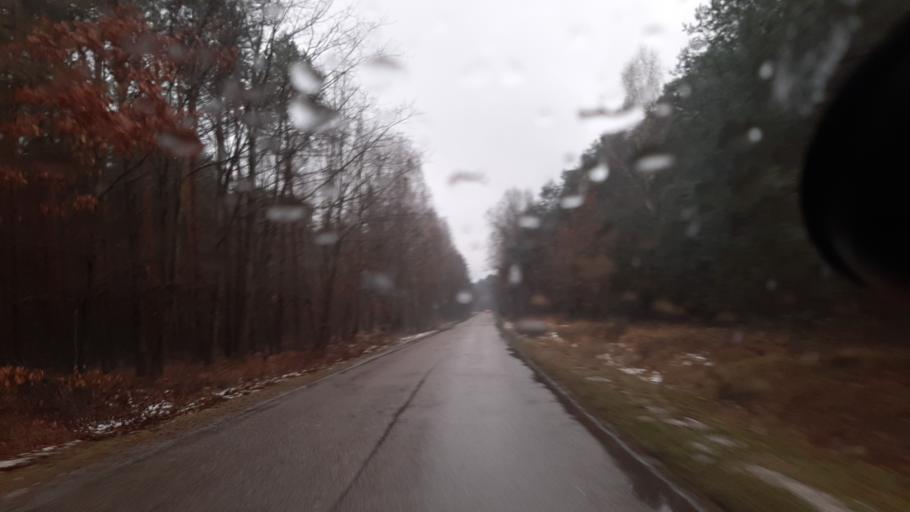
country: PL
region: Lublin Voivodeship
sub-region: Powiat lubartowski
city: Firlej
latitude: 51.5136
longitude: 22.4939
